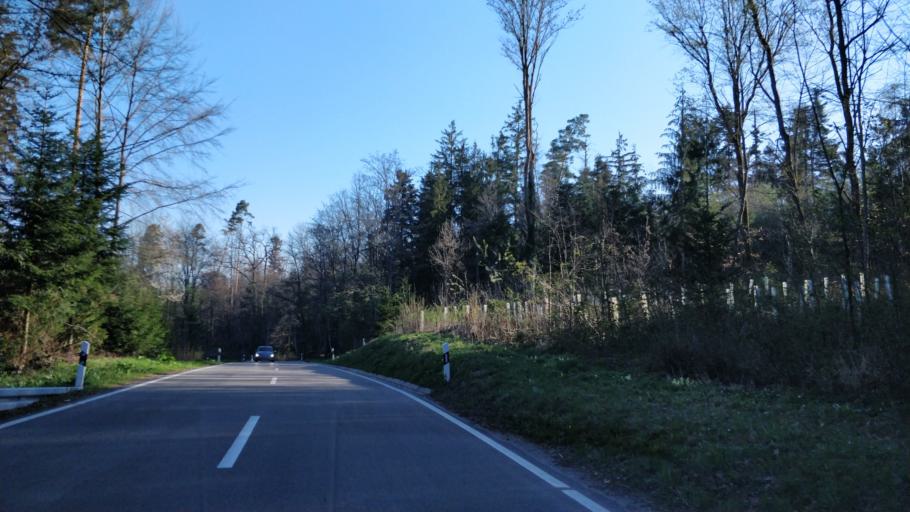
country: DE
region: Baden-Wuerttemberg
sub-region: Regierungsbezirk Stuttgart
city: Oberrot
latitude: 49.0428
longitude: 9.7068
